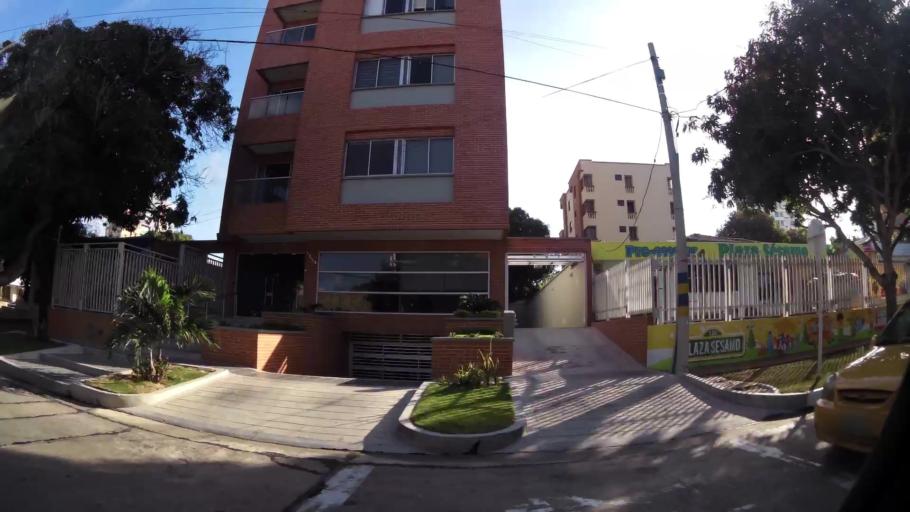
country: CO
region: Atlantico
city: Barranquilla
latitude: 11.0015
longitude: -74.8218
